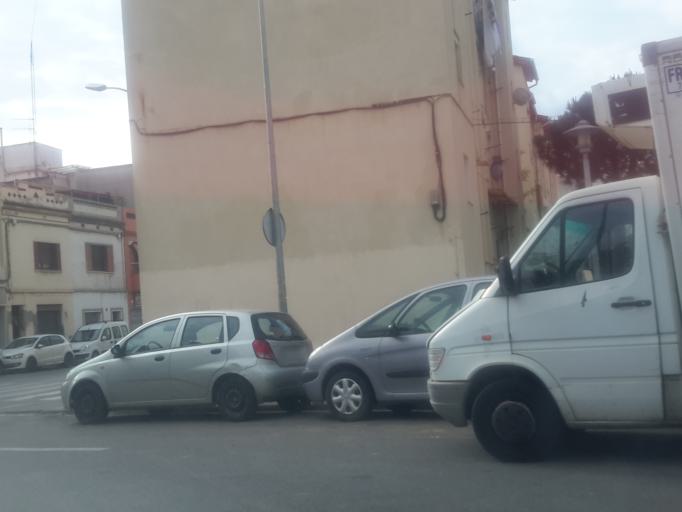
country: ES
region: Catalonia
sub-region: Provincia de Barcelona
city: Vilanova i la Geltru
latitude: 41.2244
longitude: 1.7170
